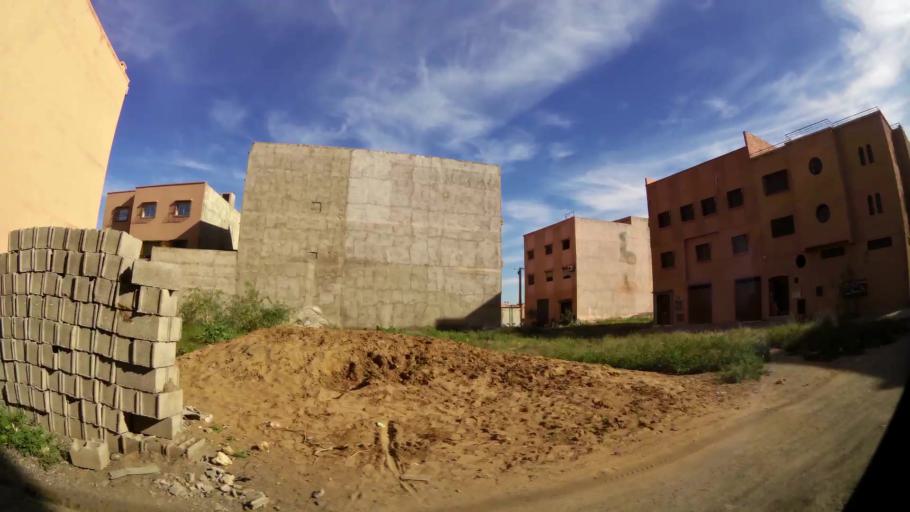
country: MA
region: Marrakech-Tensift-Al Haouz
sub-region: Marrakech
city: Marrakesh
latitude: 31.6775
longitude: -8.0403
